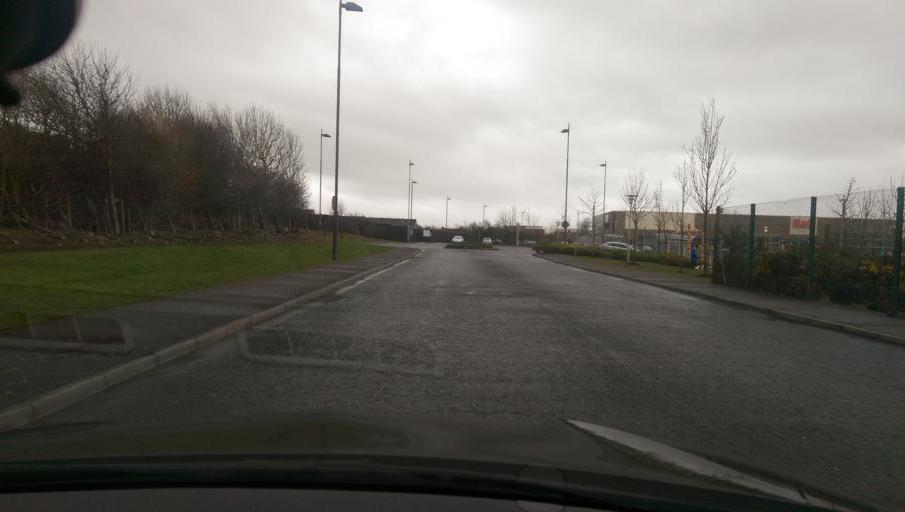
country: IE
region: Connaught
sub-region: County Galway
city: Gaillimh
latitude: 53.2730
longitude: -9.0970
